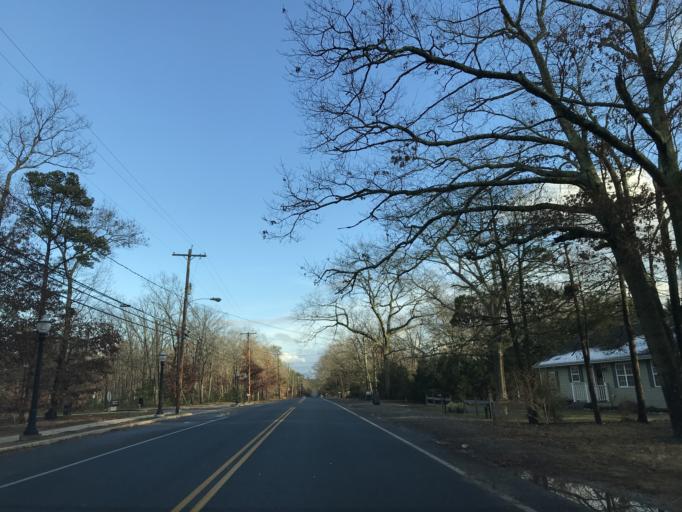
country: US
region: New Jersey
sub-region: Ocean County
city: Waretown
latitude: 39.7944
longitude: -74.2281
